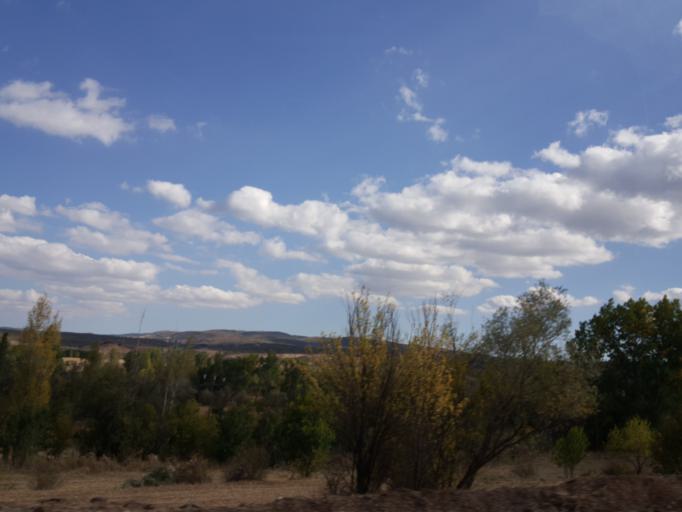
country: TR
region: Tokat
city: Sulusaray
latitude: 39.9761
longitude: 36.0189
